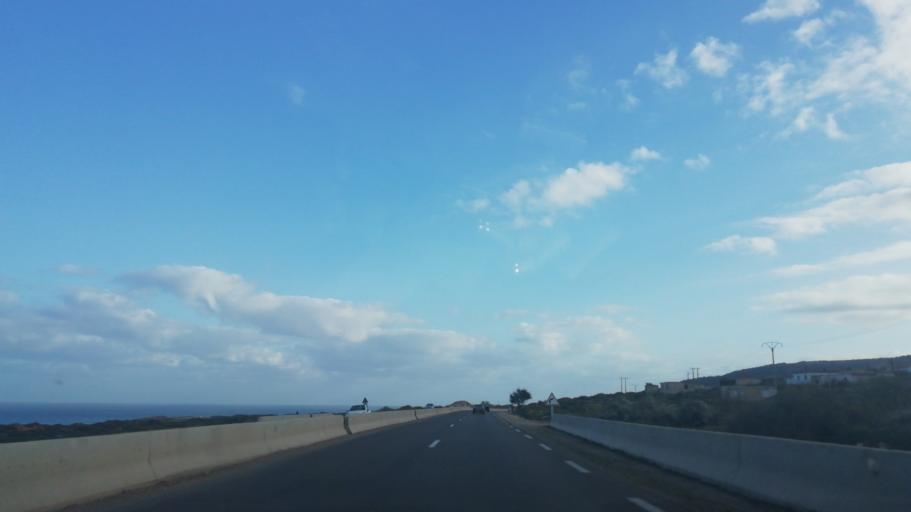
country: DZ
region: Mostaganem
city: Mostaganem
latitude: 36.0907
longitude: 0.2023
